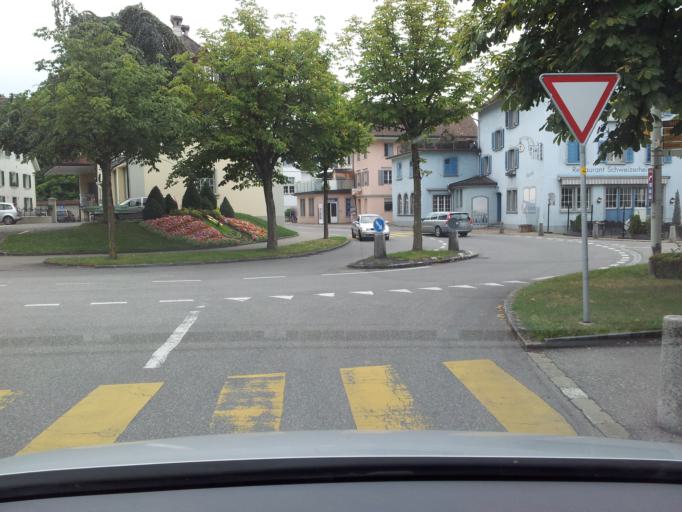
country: CH
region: Lucerne
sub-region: Sursee District
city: Sursee
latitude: 47.1716
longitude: 8.1115
